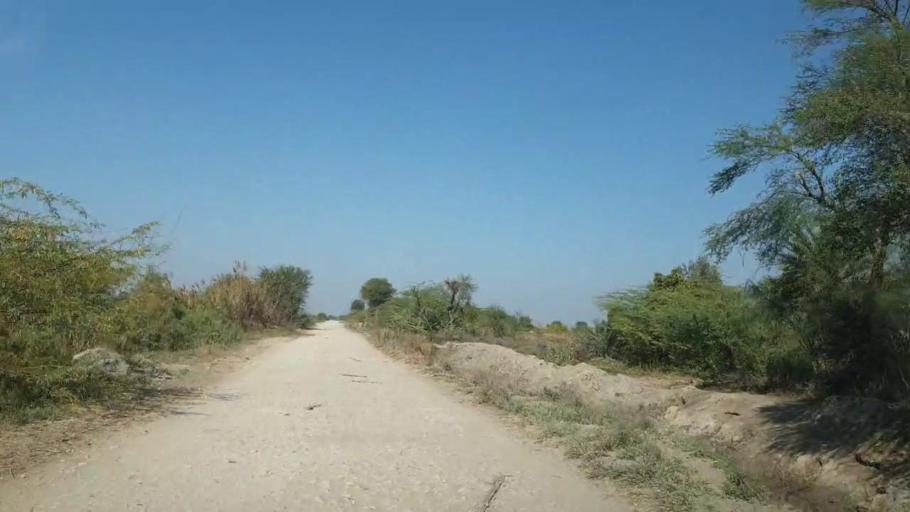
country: PK
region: Sindh
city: Mirpur Khas
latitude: 25.6623
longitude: 69.0269
